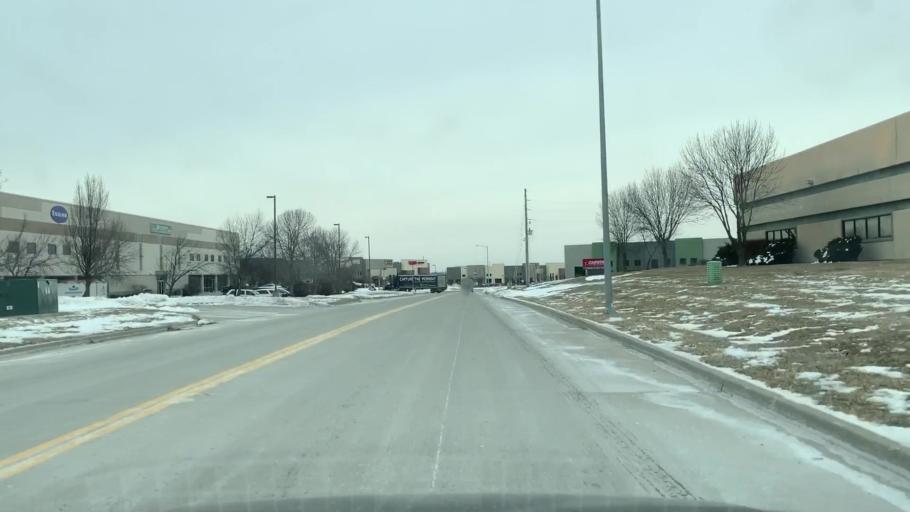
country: US
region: Missouri
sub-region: Jackson County
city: Lees Summit
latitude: 38.9579
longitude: -94.3610
